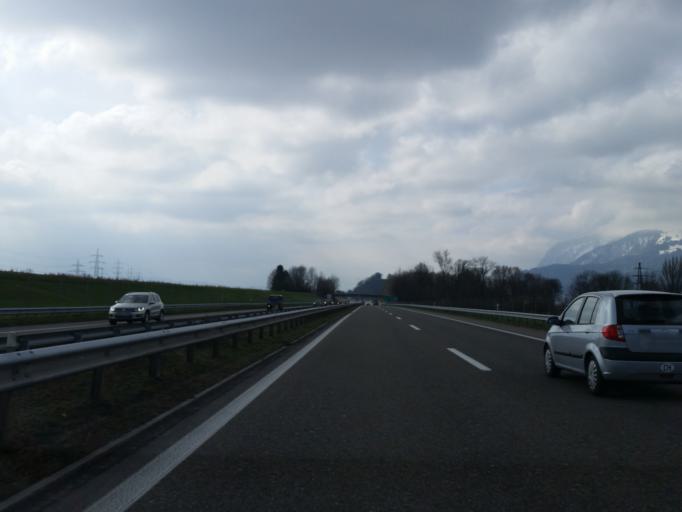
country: AT
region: Vorarlberg
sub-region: Politischer Bezirk Feldkirch
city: Mader
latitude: 47.3534
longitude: 9.6030
